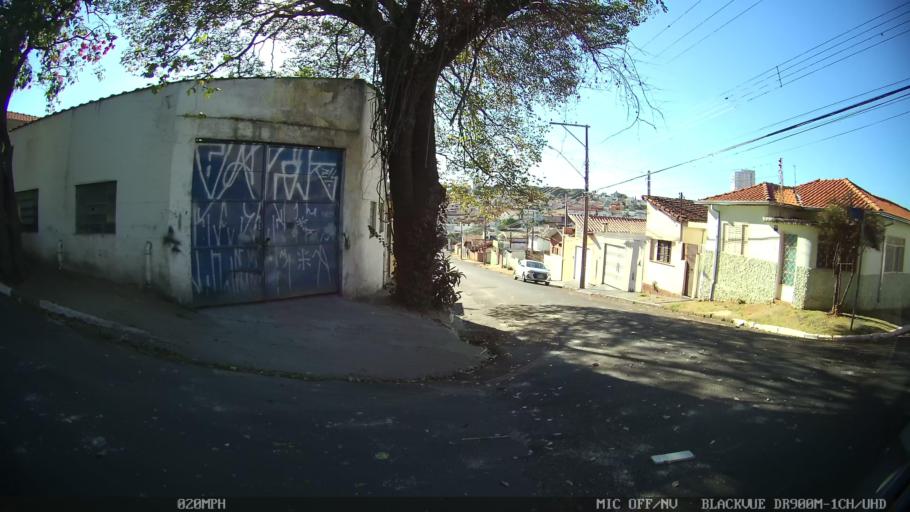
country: BR
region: Sao Paulo
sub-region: Franca
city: Franca
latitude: -20.5453
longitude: -47.4101
